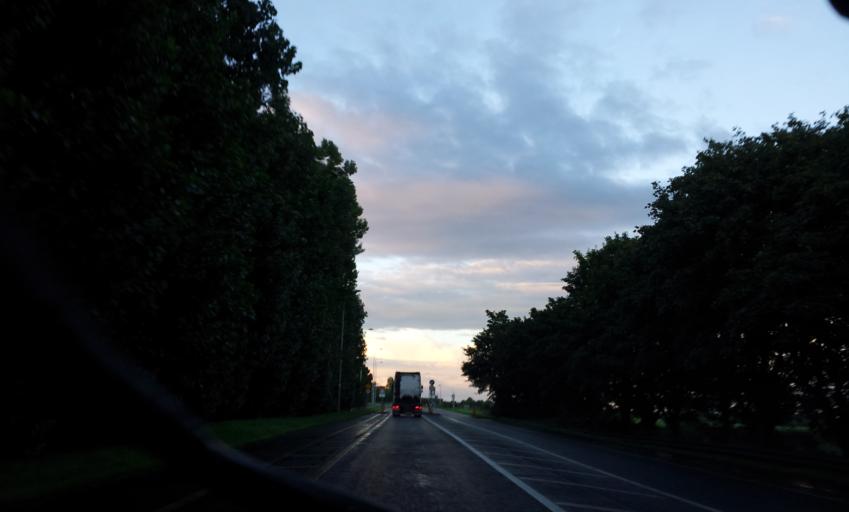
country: IE
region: Munster
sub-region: County Limerick
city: Rathkeale
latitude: 52.5349
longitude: -8.8680
